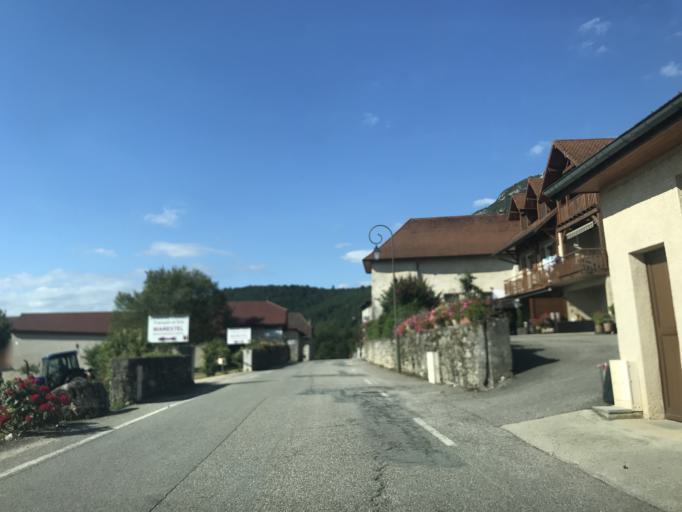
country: FR
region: Rhone-Alpes
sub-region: Departement de la Savoie
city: Yenne
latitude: 45.7319
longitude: 5.8018
